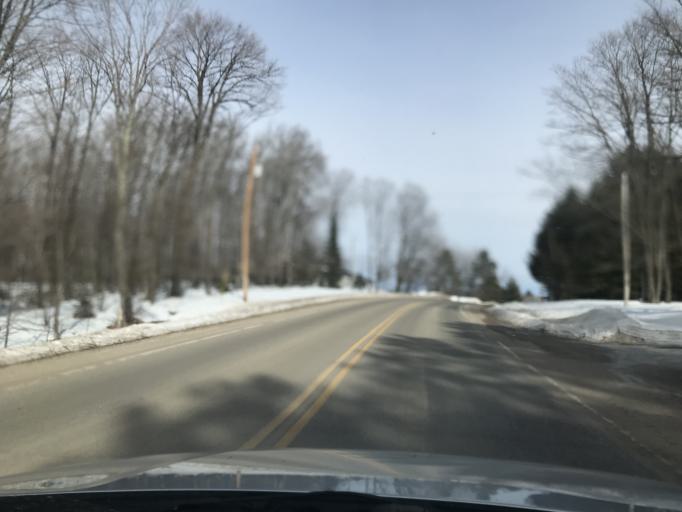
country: US
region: Wisconsin
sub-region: Marinette County
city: Peshtigo
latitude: 45.2807
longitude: -87.7686
